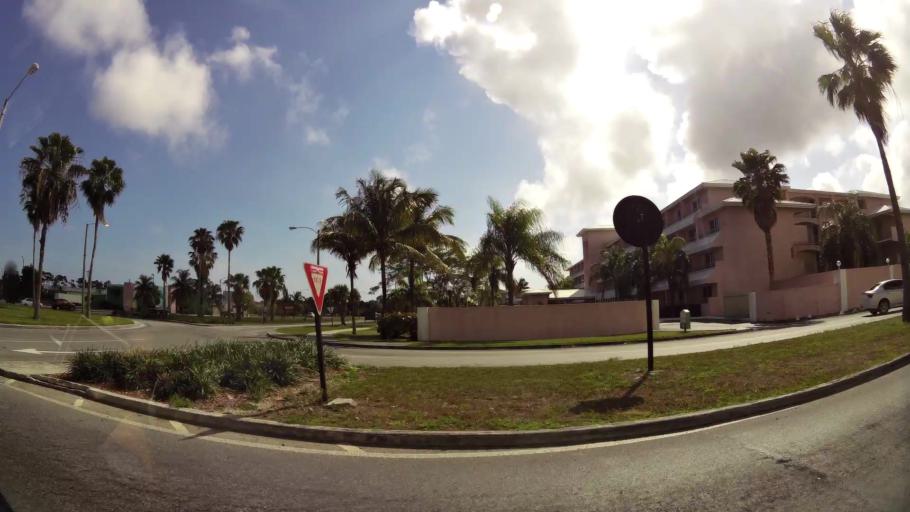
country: BS
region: Freeport
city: Freeport
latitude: 26.5204
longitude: -78.6950
